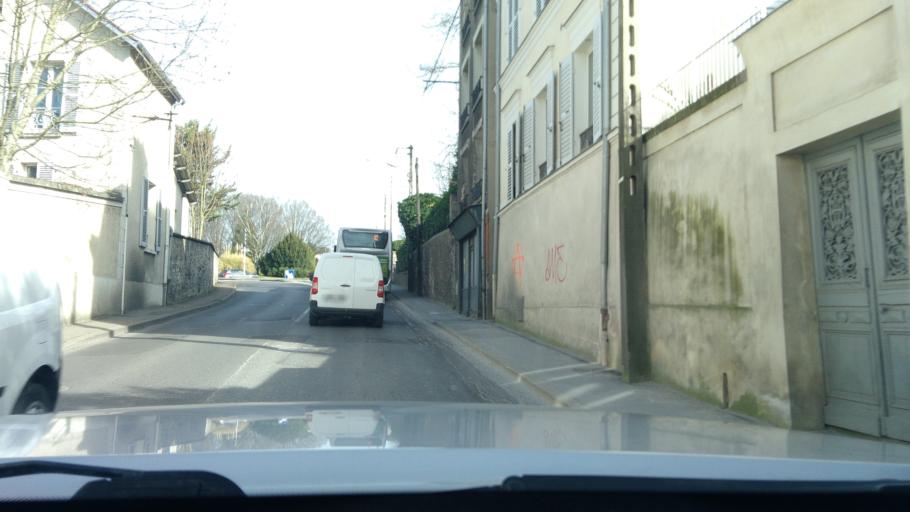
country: FR
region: Ile-de-France
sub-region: Departement de Seine-et-Marne
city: Melun
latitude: 48.5408
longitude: 2.6708
